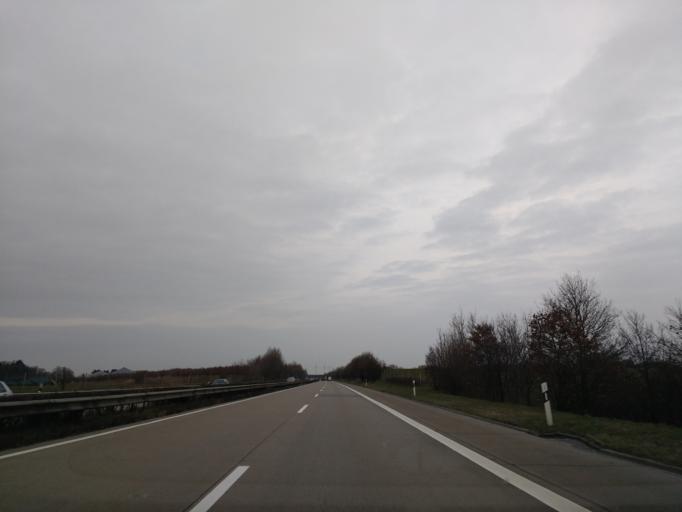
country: DE
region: Lower Saxony
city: Langen
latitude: 53.6359
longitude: 8.6647
